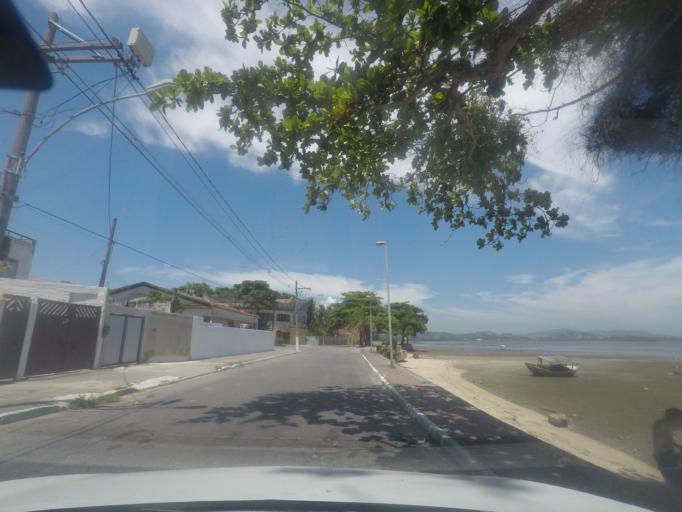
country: BR
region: Rio de Janeiro
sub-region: Itaguai
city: Itaguai
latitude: -22.9846
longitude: -43.6853
